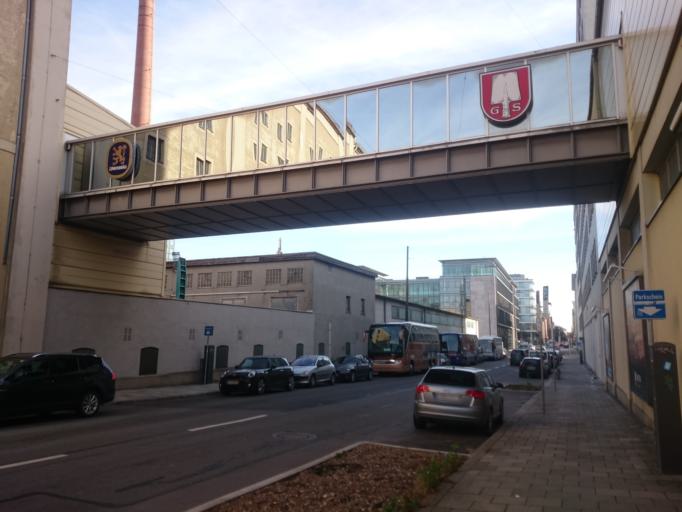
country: DE
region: Bavaria
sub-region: Upper Bavaria
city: Munich
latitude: 48.1464
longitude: 11.5550
